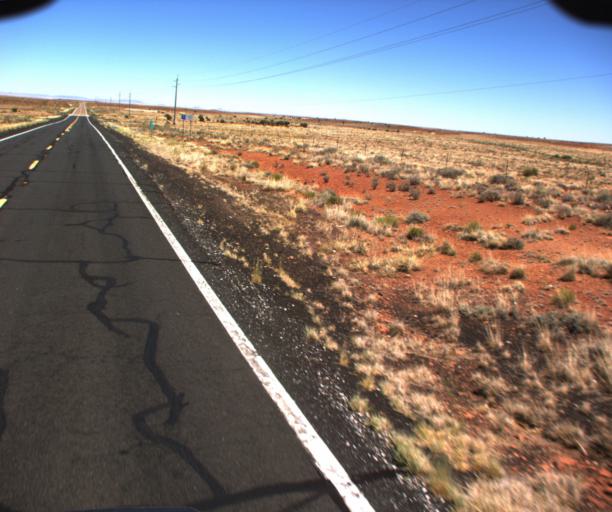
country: US
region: Arizona
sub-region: Coconino County
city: LeChee
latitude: 34.9048
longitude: -110.8460
